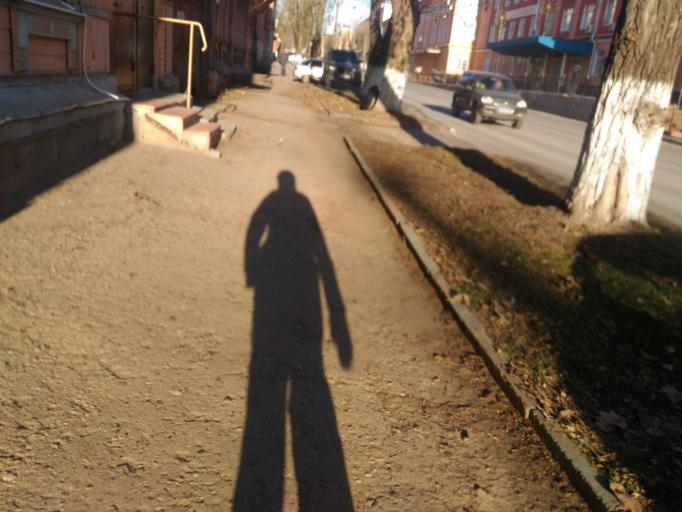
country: RU
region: Ulyanovsk
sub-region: Ulyanovskiy Rayon
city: Ulyanovsk
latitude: 54.3185
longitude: 48.3844
